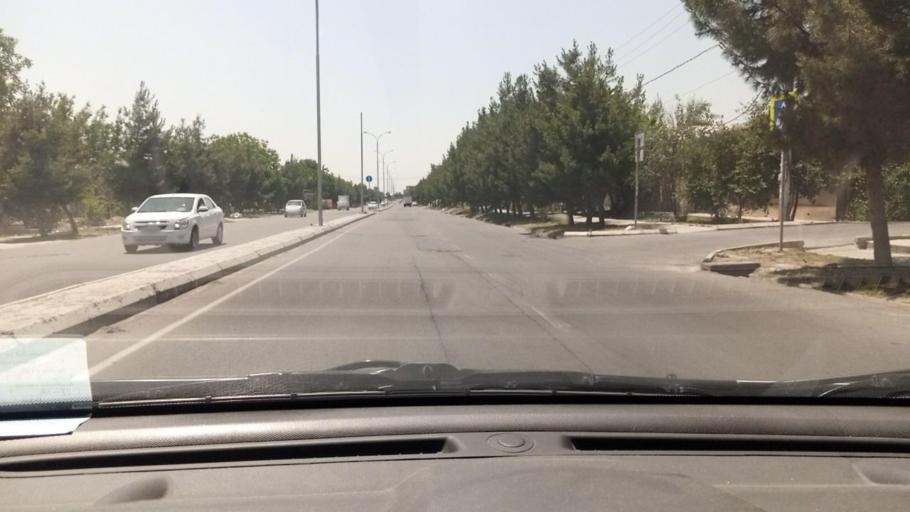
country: UZ
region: Toshkent Shahri
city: Tashkent
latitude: 41.2344
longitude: 69.1872
